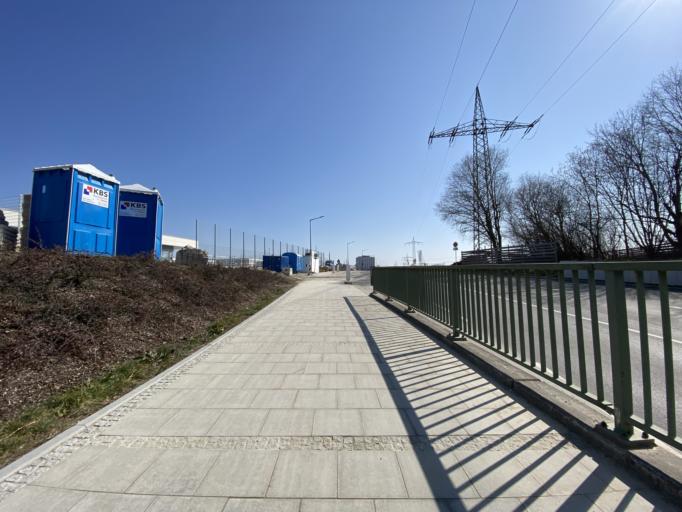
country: DE
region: Bavaria
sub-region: Upper Bavaria
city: Unterfoehring
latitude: 48.1852
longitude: 11.6447
